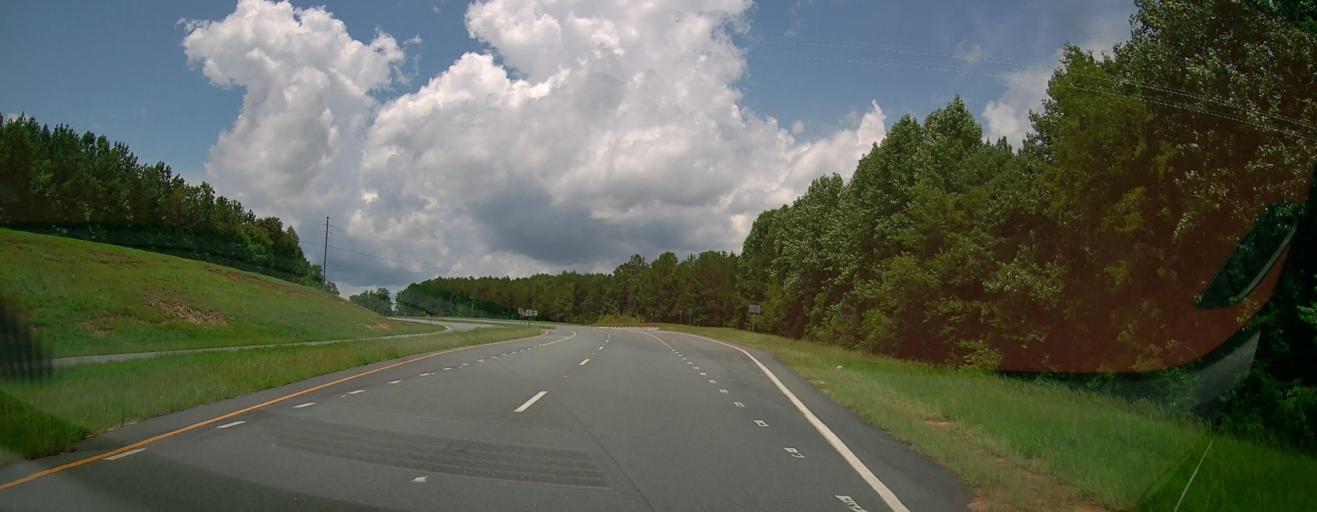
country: US
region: Georgia
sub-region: Upson County
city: Thomaston
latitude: 32.7871
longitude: -84.2481
